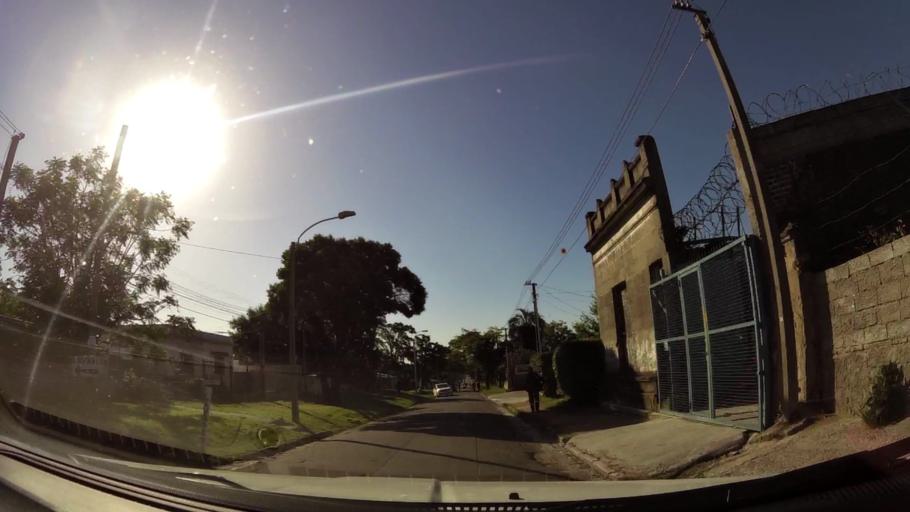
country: UY
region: Canelones
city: La Paz
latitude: -34.8193
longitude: -56.2208
